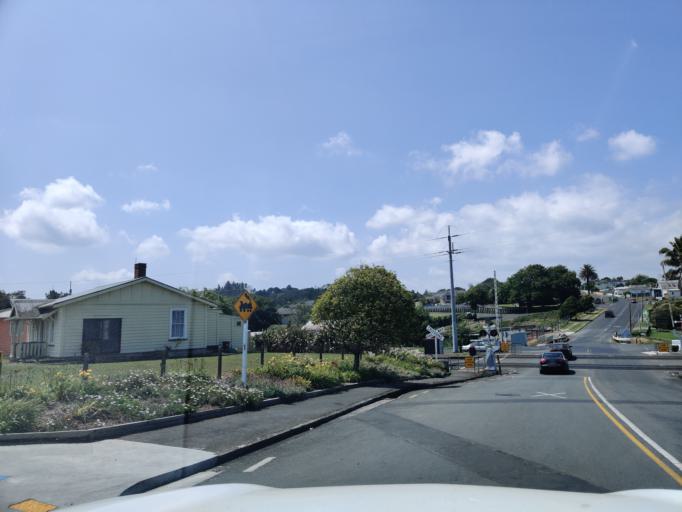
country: NZ
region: Auckland
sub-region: Auckland
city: Pukekohe East
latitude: -37.2570
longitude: 174.9472
